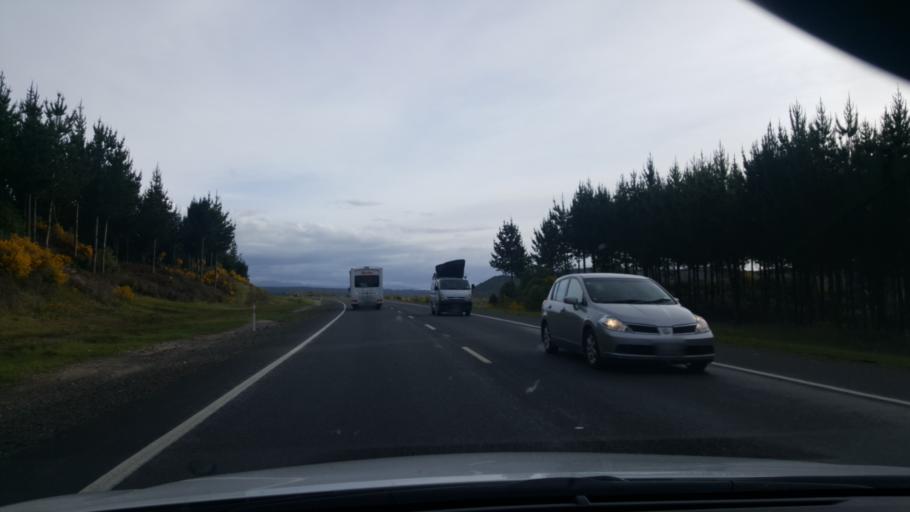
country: NZ
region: Waikato
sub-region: Taupo District
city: Taupo
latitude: -38.8283
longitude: 176.0667
